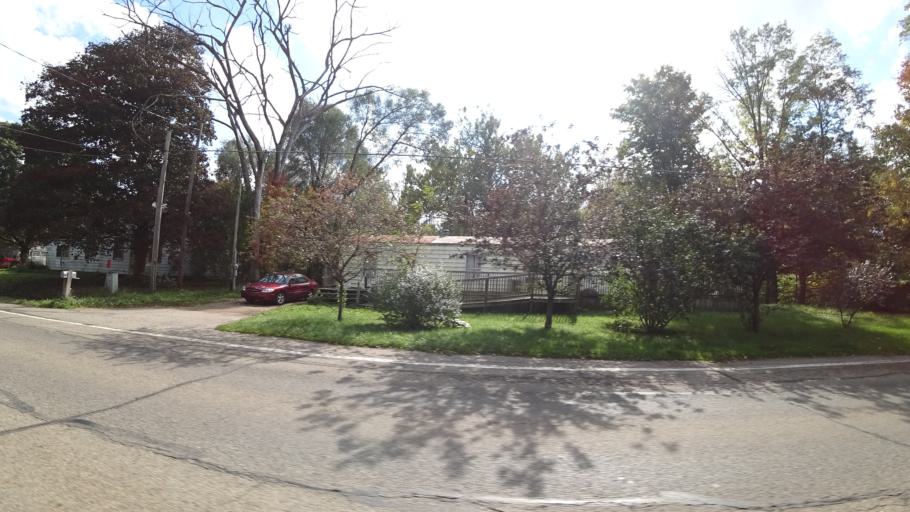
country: US
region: Michigan
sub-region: Branch County
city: Union City
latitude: 42.1062
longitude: -85.0683
